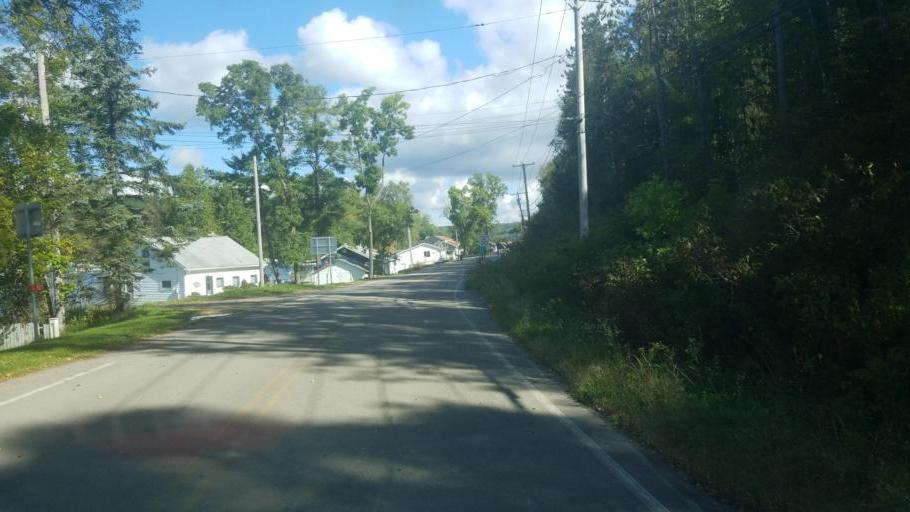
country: US
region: New York
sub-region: Allegany County
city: Cuba
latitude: 42.2386
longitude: -78.3058
